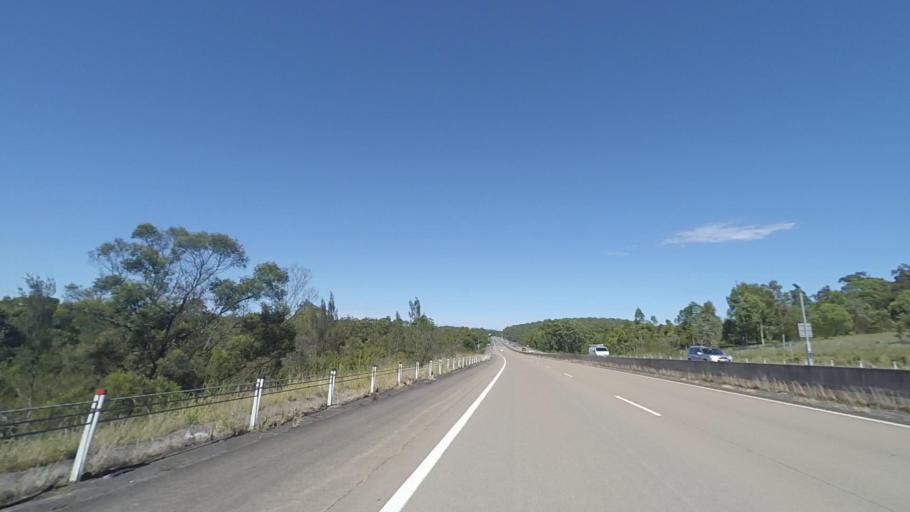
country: AU
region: New South Wales
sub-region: Port Stephens Shire
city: Port Stephens
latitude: -32.6207
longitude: 151.9663
